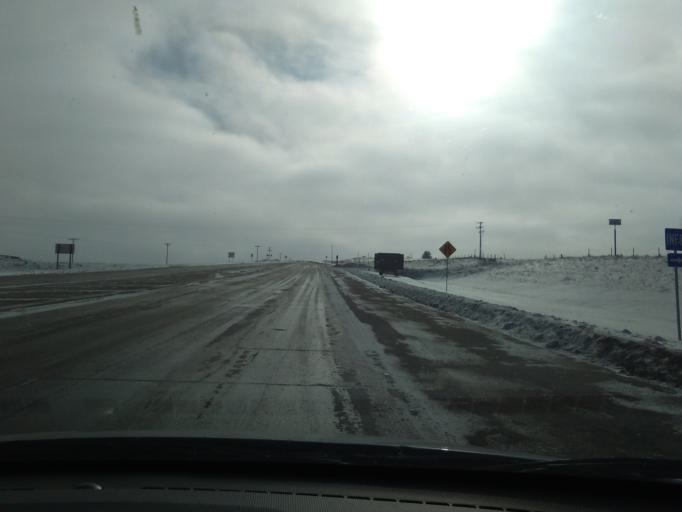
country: US
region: Nebraska
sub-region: Kimball County
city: Kimball
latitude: 41.2151
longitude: -103.6634
